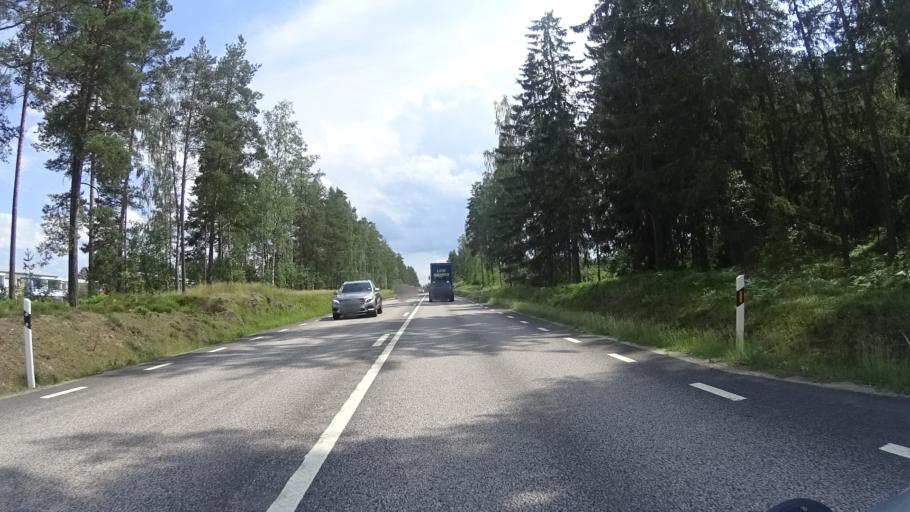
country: SE
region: Kalmar
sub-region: Hultsfreds Kommun
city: Hultsfred
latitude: 57.4809
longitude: 15.8334
